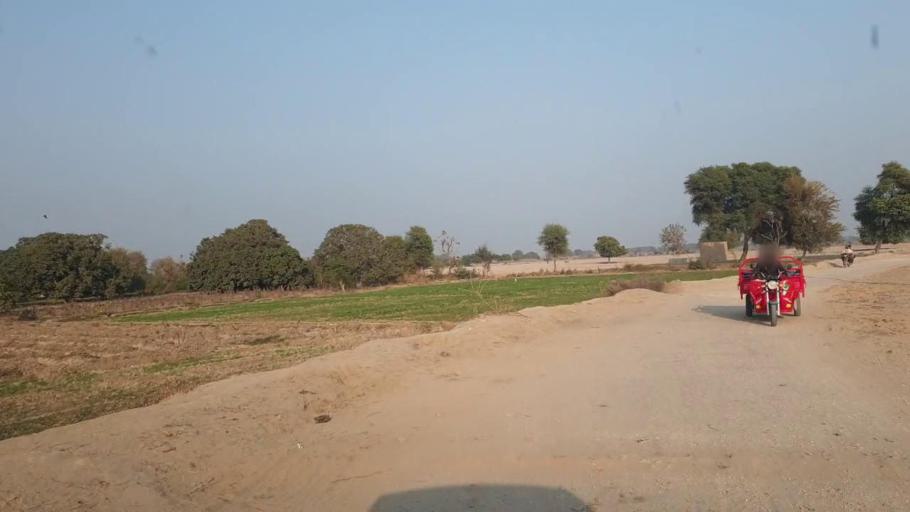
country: PK
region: Sindh
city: Hala
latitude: 25.8113
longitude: 68.4389
